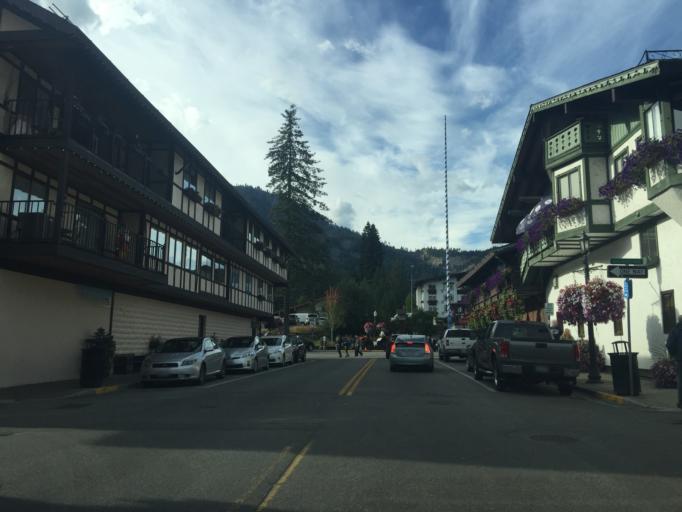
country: US
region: Washington
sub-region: Chelan County
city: Leavenworth
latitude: 47.5947
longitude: -120.6618
